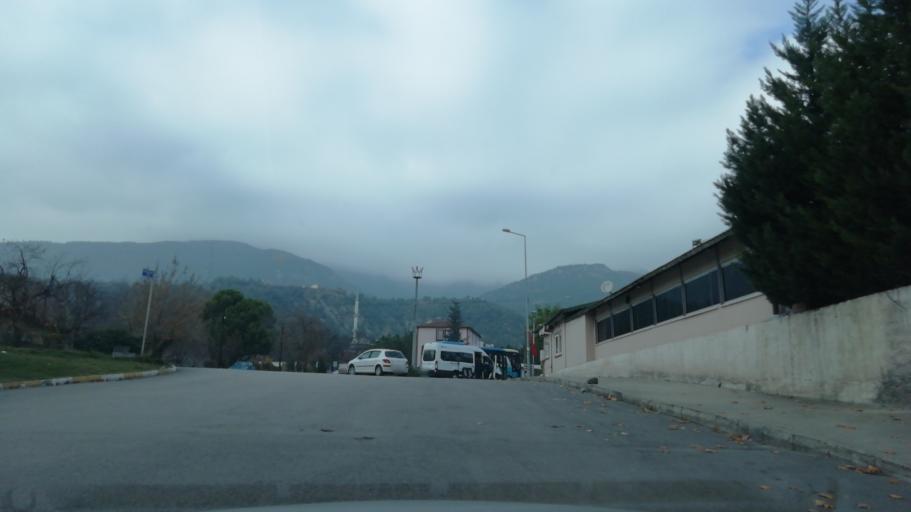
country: TR
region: Karabuk
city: Karabuk
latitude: 41.2064
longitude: 32.6203
